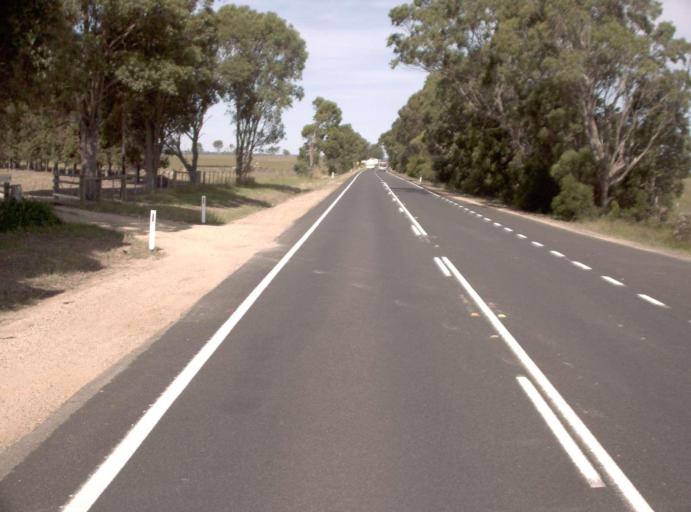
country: AU
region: Victoria
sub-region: East Gippsland
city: Bairnsdale
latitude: -37.8198
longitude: 147.7702
